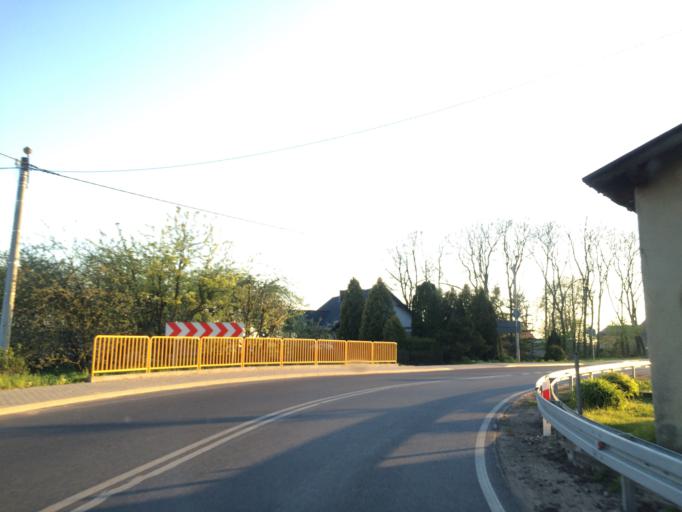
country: PL
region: Warmian-Masurian Voivodeship
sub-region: Powiat ilawski
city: Lubawa
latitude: 53.5060
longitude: 19.8564
